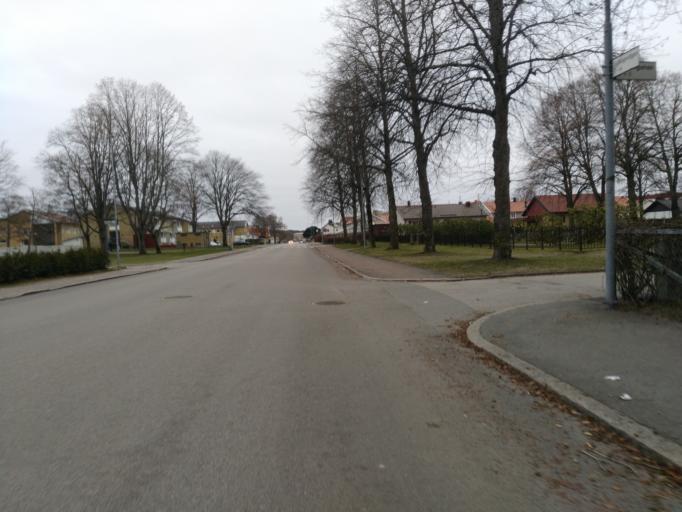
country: SE
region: Vaestra Goetaland
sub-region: Lidkopings Kommun
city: Lidkoping
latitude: 58.4981
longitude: 13.1611
